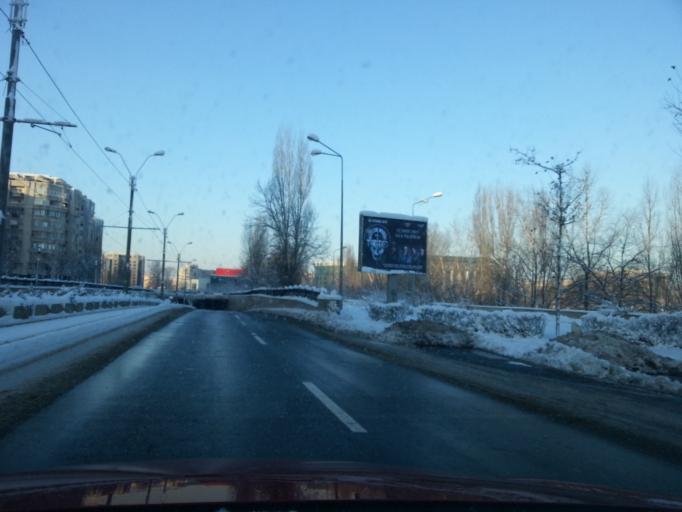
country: RO
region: Bucuresti
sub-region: Municipiul Bucuresti
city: Bucharest
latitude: 44.4239
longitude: 26.1163
